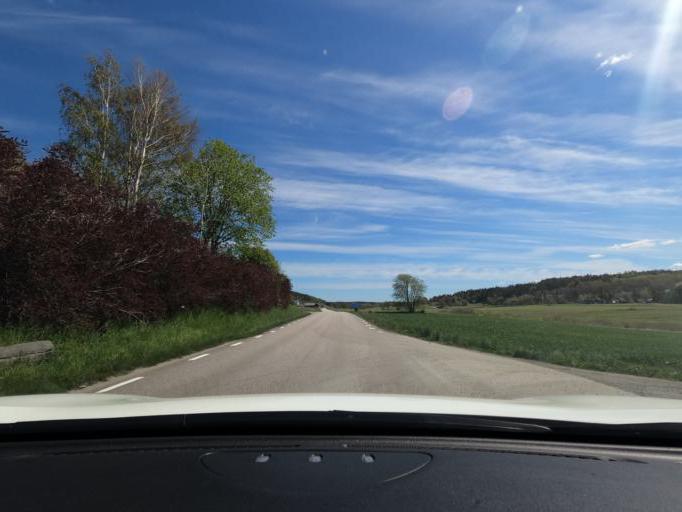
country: SE
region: Halland
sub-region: Kungsbacka Kommun
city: Fjaeras kyrkby
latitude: 57.4223
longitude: 12.3195
